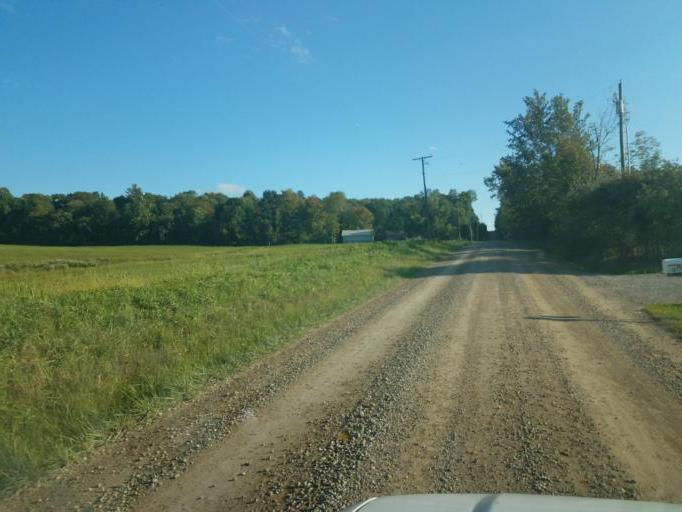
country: US
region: Ohio
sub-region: Knox County
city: Mount Vernon
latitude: 40.3958
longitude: -82.5641
